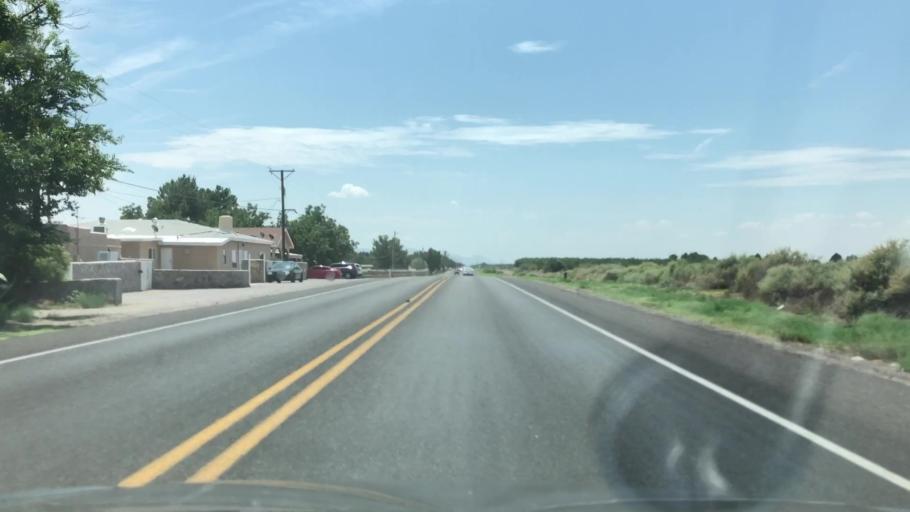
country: US
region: New Mexico
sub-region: Dona Ana County
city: Mesquite
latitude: 32.2004
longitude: -106.7193
